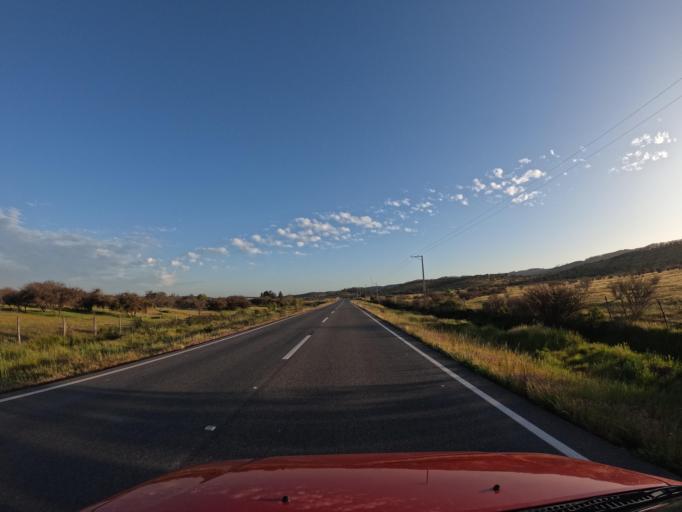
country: CL
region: O'Higgins
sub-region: Provincia de Colchagua
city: Santa Cruz
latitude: -34.3221
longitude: -71.7437
